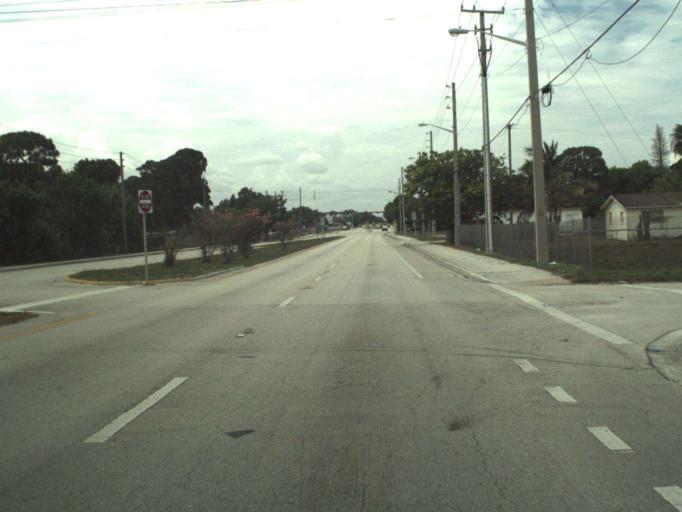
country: US
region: Florida
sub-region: Saint Lucie County
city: Fort Pierce North
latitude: 27.4686
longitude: -80.3498
